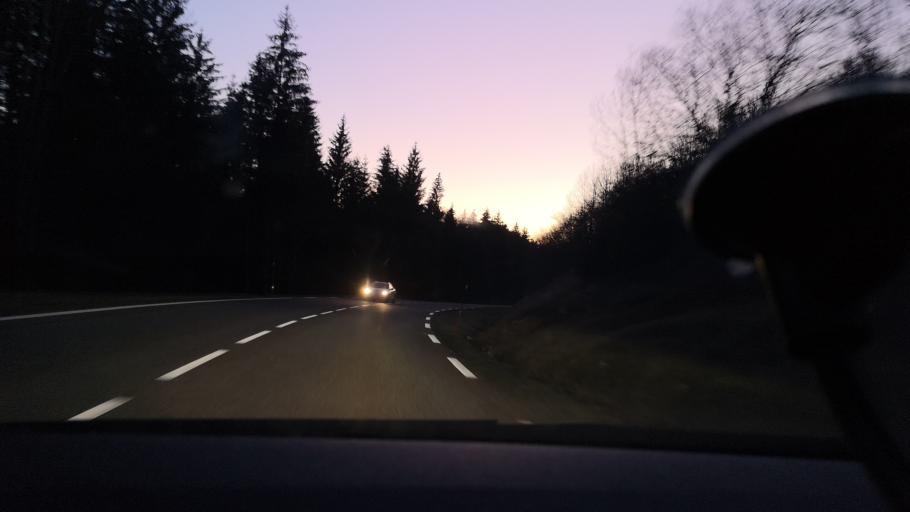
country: FR
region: Franche-Comte
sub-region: Departement du Jura
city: Champagnole
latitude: 46.7767
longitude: 5.9969
